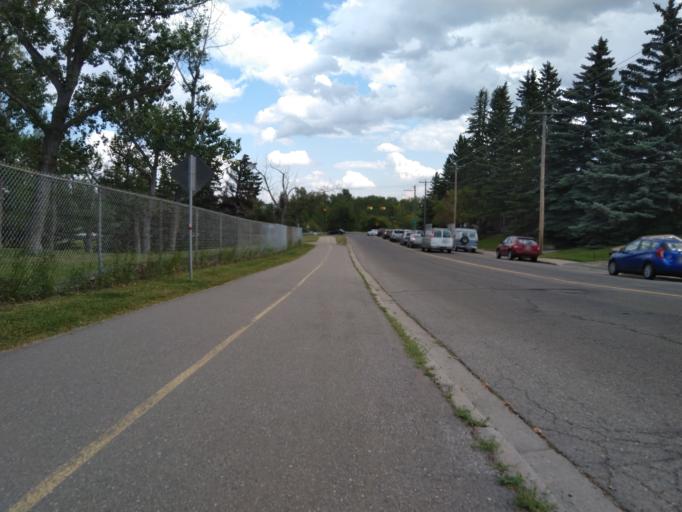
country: CA
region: Alberta
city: Calgary
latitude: 51.0743
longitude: -114.0967
